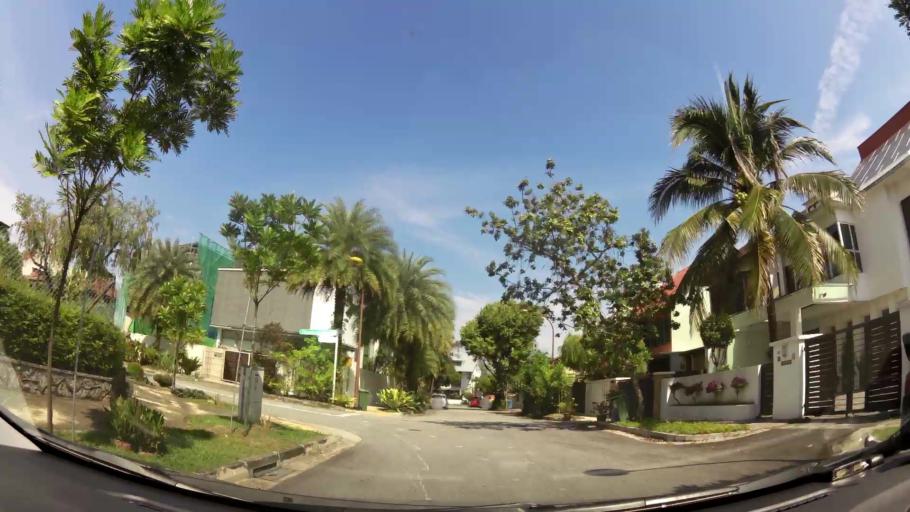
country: SG
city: Singapore
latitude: 1.3796
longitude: 103.8337
